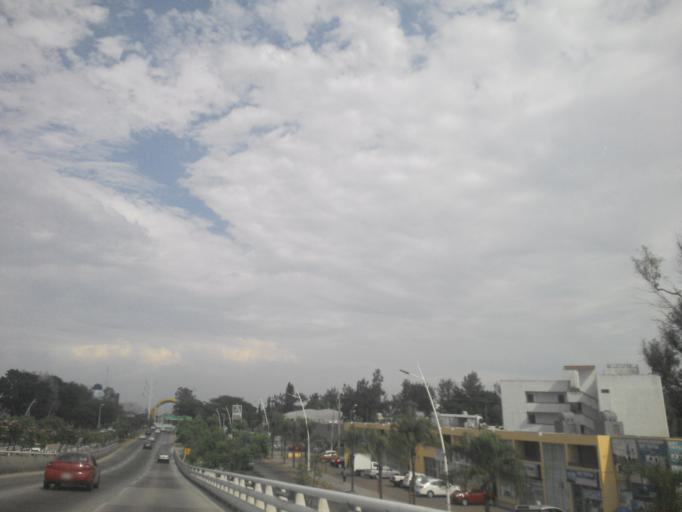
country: MX
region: Jalisco
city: Guadalajara
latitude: 20.6638
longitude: -103.3921
